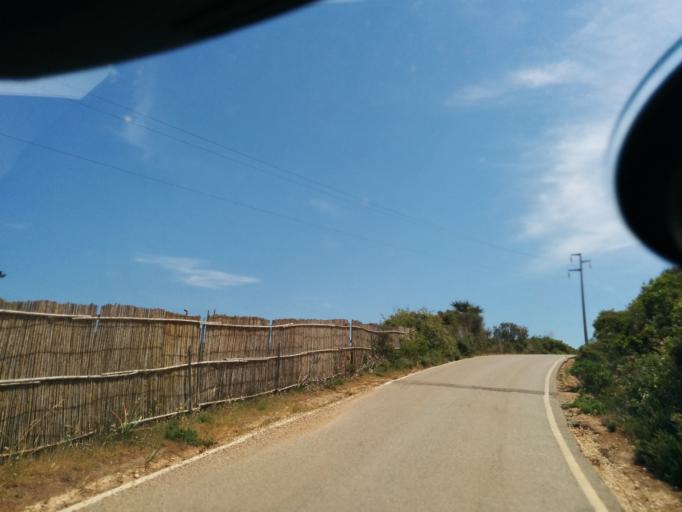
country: IT
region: Sardinia
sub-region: Provincia di Carbonia-Iglesias
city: Calasetta
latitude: 39.0207
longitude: 8.3802
